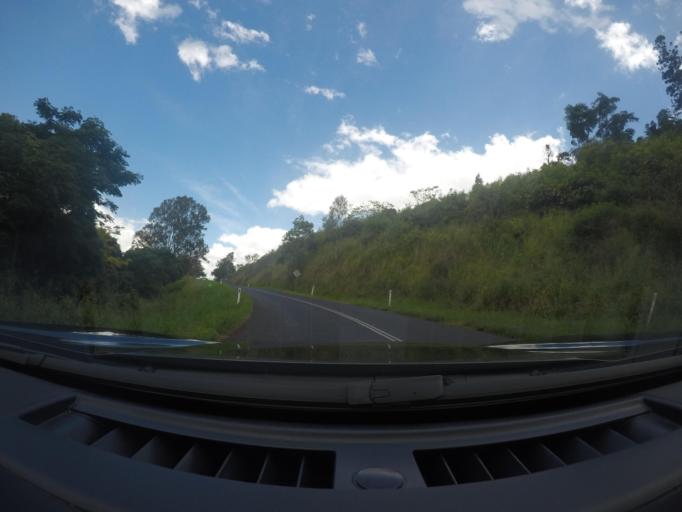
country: AU
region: Queensland
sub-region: Moreton Bay
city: Woodford
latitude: -27.0873
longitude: 152.5602
